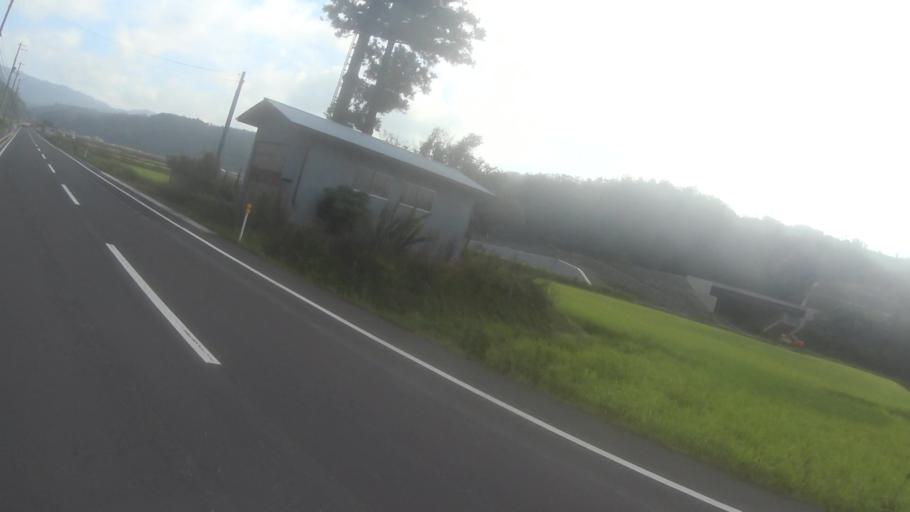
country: JP
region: Kyoto
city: Miyazu
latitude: 35.5757
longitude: 135.1194
